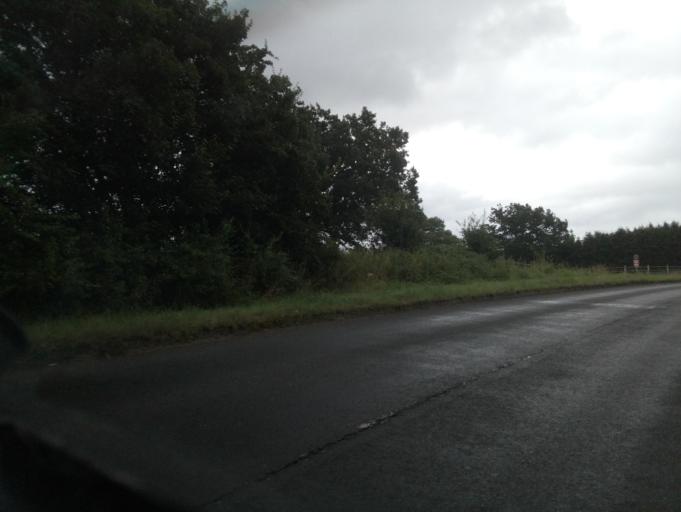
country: GB
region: England
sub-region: Solihull
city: Cheswick Green
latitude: 52.3855
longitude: -1.8226
